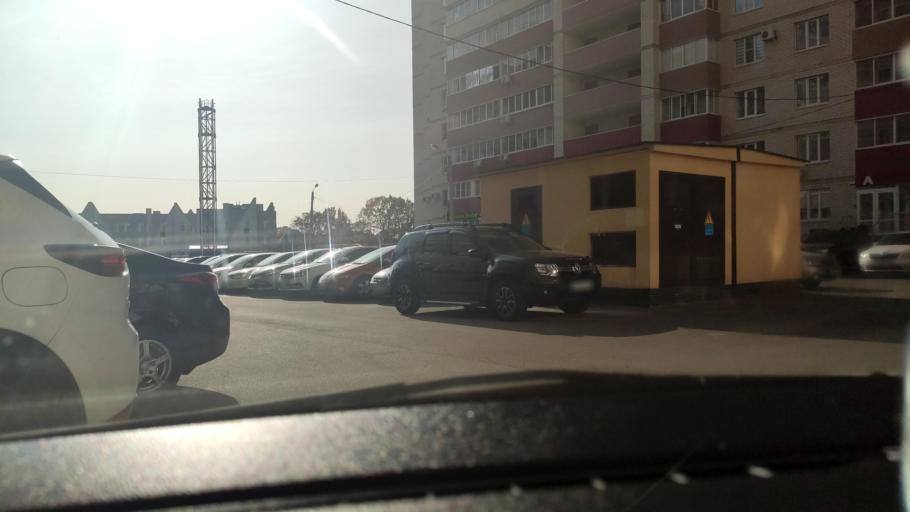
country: RU
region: Voronezj
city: Voronezh
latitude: 51.7127
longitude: 39.1987
